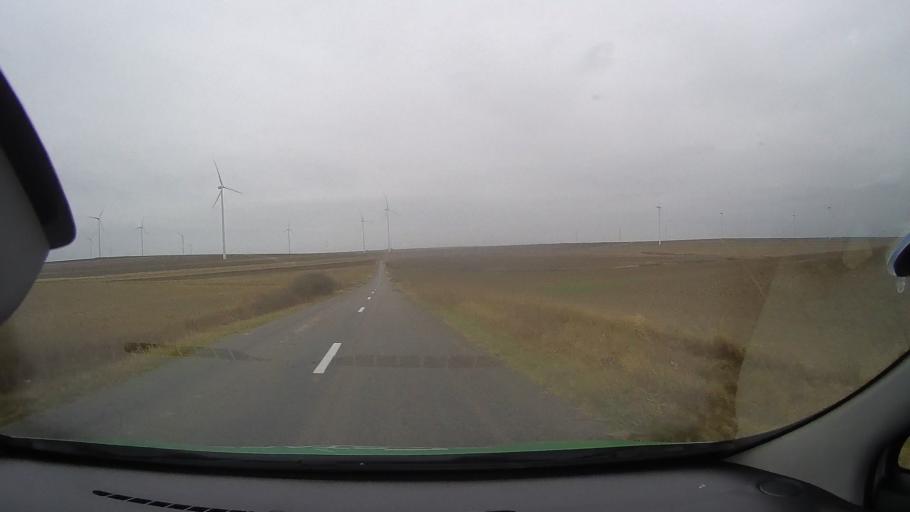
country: RO
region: Constanta
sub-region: Comuna Pantelimon
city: Pantelimon
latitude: 44.5131
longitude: 28.3350
